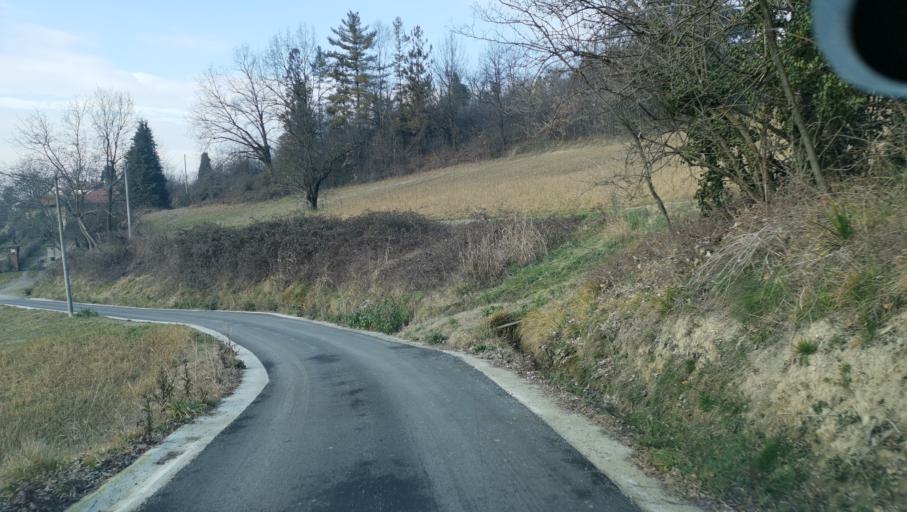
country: IT
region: Piedmont
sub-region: Provincia di Torino
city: Gassino Torinese
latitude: 45.1127
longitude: 7.8392
